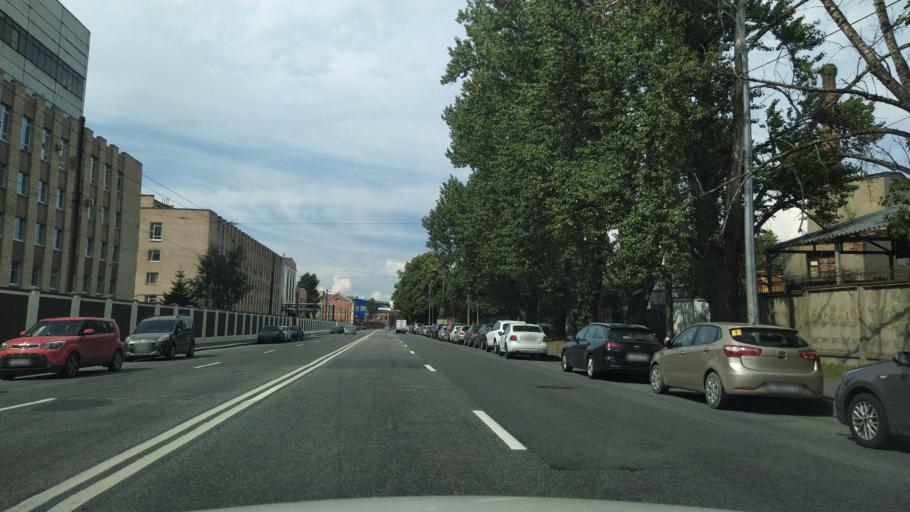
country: RU
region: Leningrad
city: Finlyandskiy
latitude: 59.9579
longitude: 30.3717
